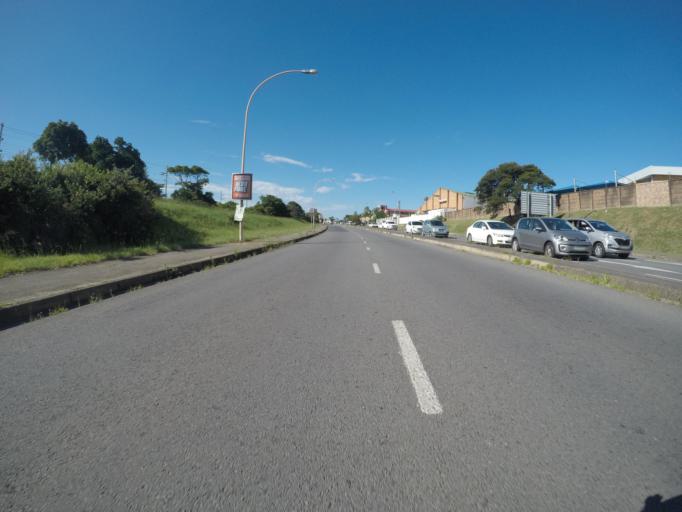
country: ZA
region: Eastern Cape
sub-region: Buffalo City Metropolitan Municipality
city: East London
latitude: -32.9837
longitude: 27.8978
